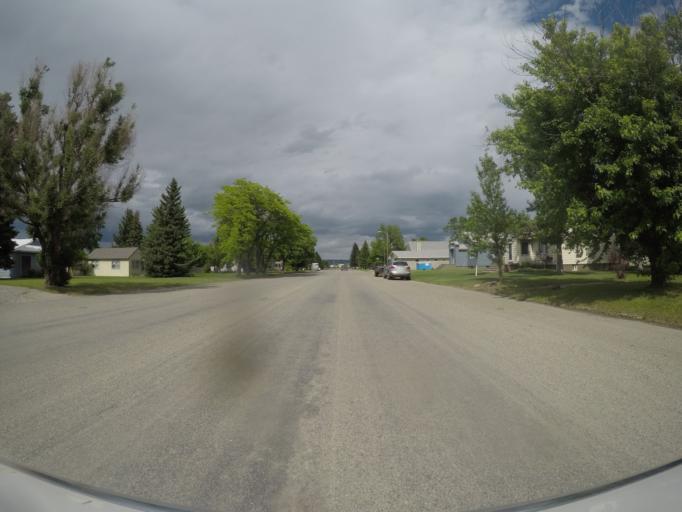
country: US
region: Montana
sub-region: Sweet Grass County
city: Big Timber
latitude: 45.8356
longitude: -109.9474
